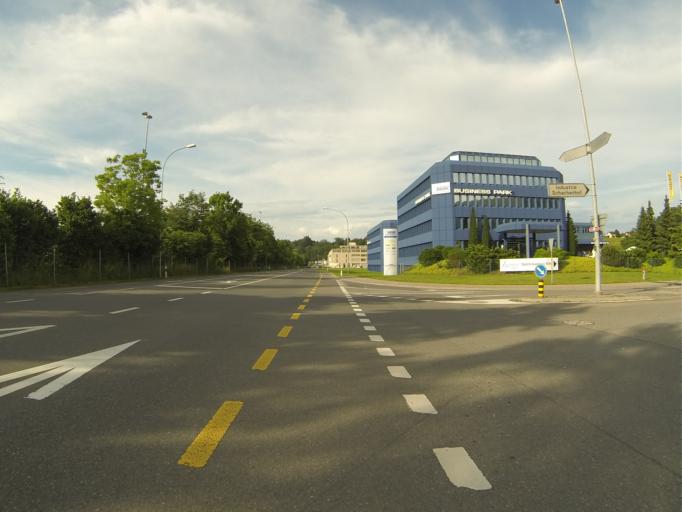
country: CH
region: Lucerne
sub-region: Lucerne-Stadt District
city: Littau
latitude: 47.0624
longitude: 8.2645
